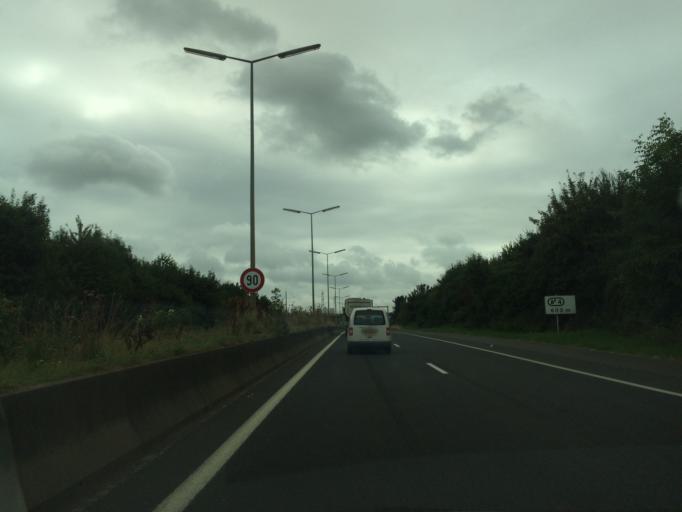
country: LU
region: Luxembourg
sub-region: Canton d'Esch-sur-Alzette
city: Mondercange
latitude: 49.5214
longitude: 5.9703
